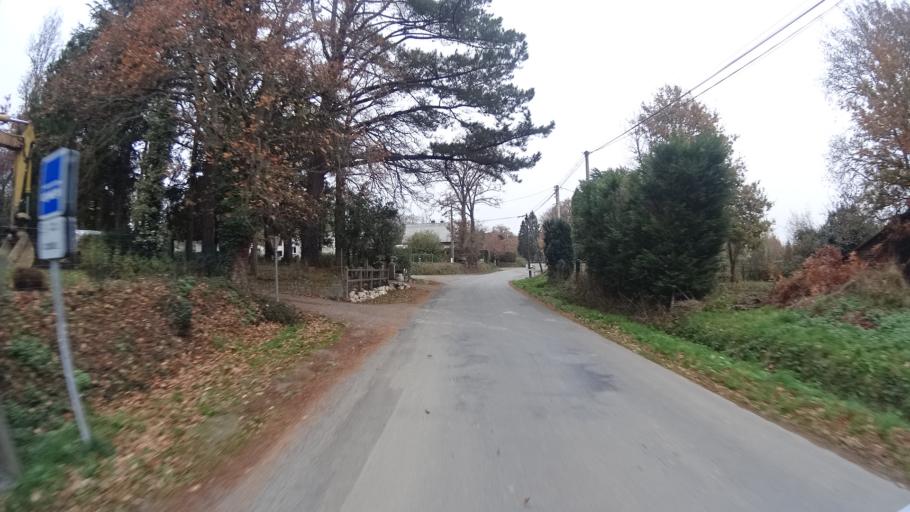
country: FR
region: Brittany
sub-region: Departement d'Ille-et-Vilaine
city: Bains-sur-Oust
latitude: 47.6857
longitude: -2.0785
